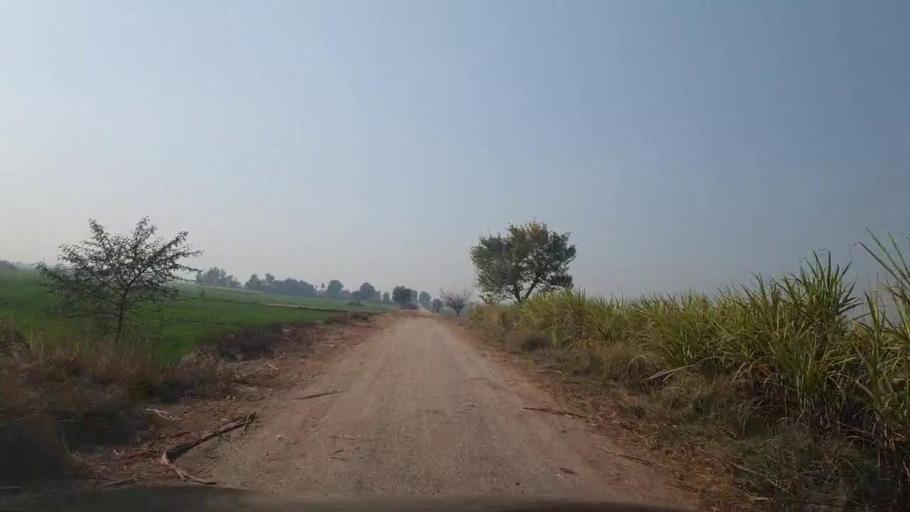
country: PK
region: Sindh
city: Ubauro
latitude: 28.1233
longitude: 69.8156
